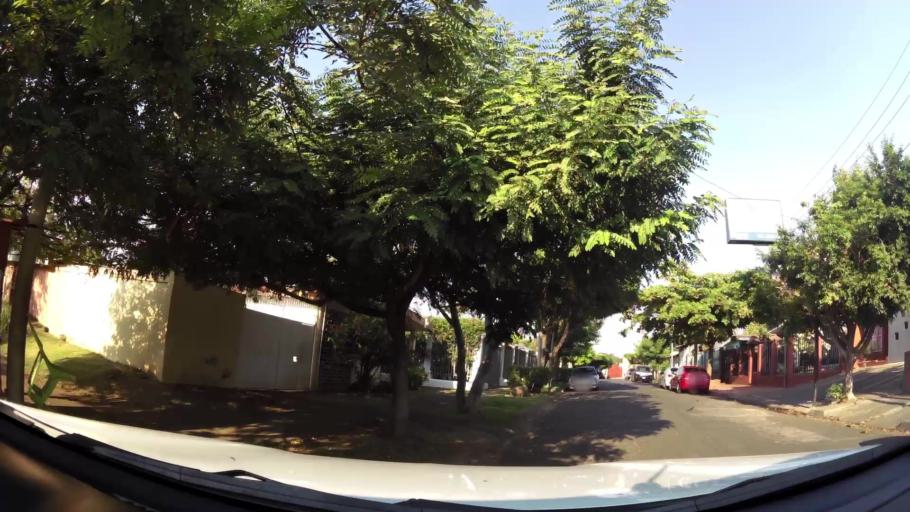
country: NI
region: Managua
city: Managua
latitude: 12.1230
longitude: -86.2566
